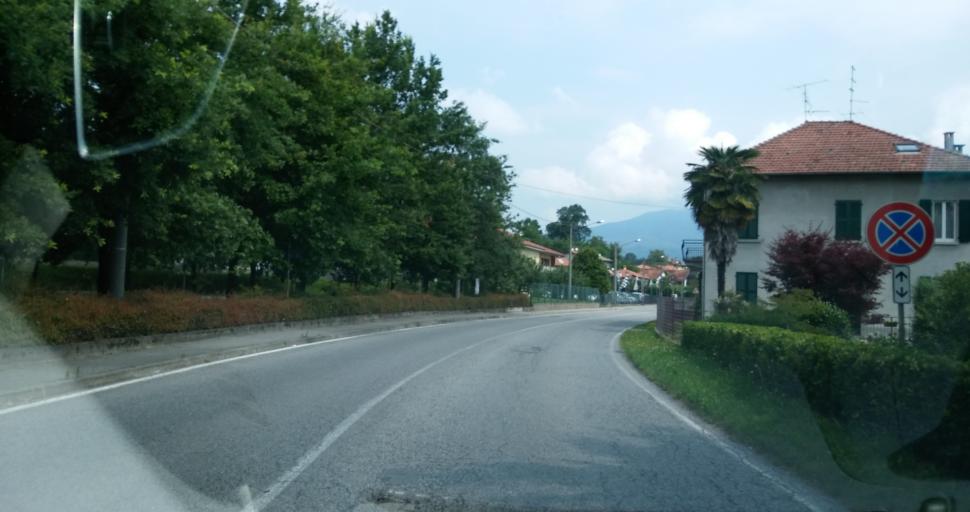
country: IT
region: Lombardy
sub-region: Provincia di Varese
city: Biandronno
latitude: 45.8006
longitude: 8.7045
